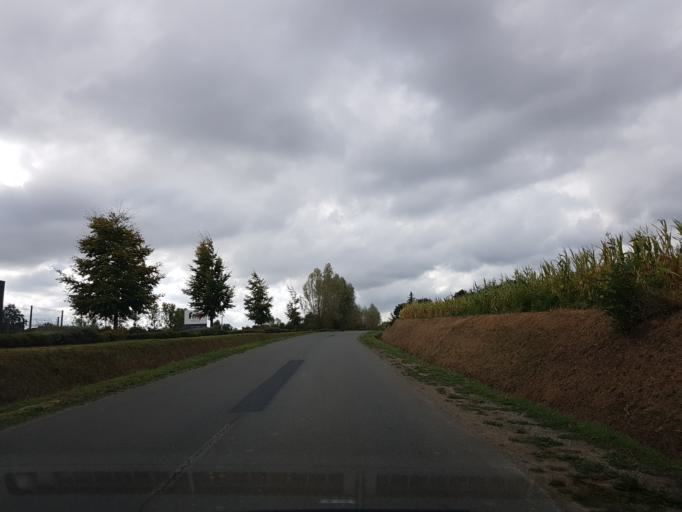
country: FR
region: Brittany
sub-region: Departement des Cotes-d'Armor
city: Quessoy
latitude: 48.4449
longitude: -2.6475
